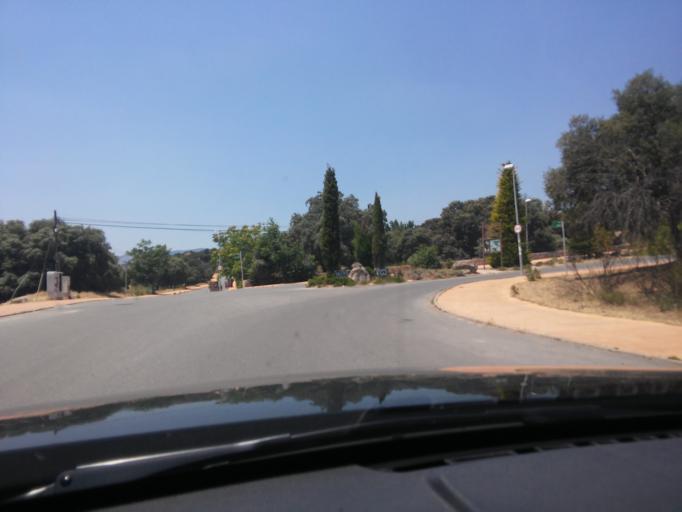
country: ES
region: Madrid
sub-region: Provincia de Madrid
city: Navalquejigo
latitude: 40.6097
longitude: -4.0474
